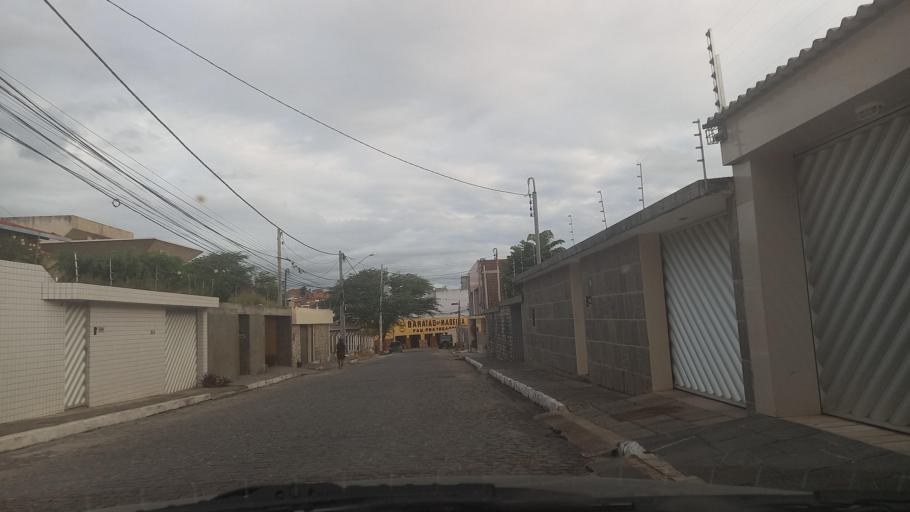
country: BR
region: Pernambuco
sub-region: Caruaru
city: Caruaru
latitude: -8.2713
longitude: -35.9634
